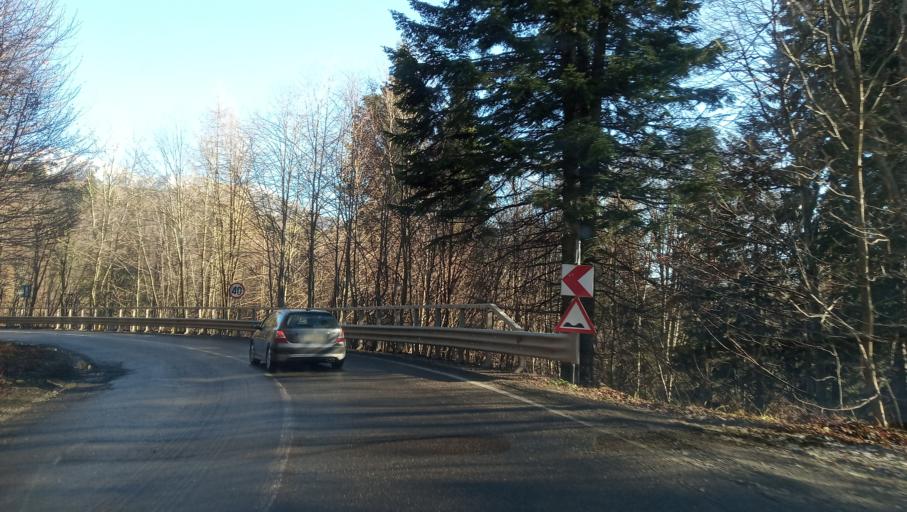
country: RO
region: Brasov
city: Crivina
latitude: 45.4698
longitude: 25.9257
